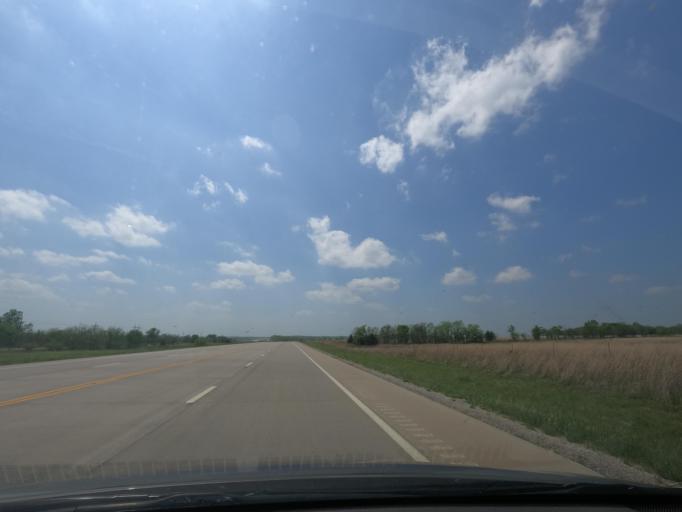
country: US
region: Kansas
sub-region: Elk County
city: Howard
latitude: 37.6359
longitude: -96.1689
